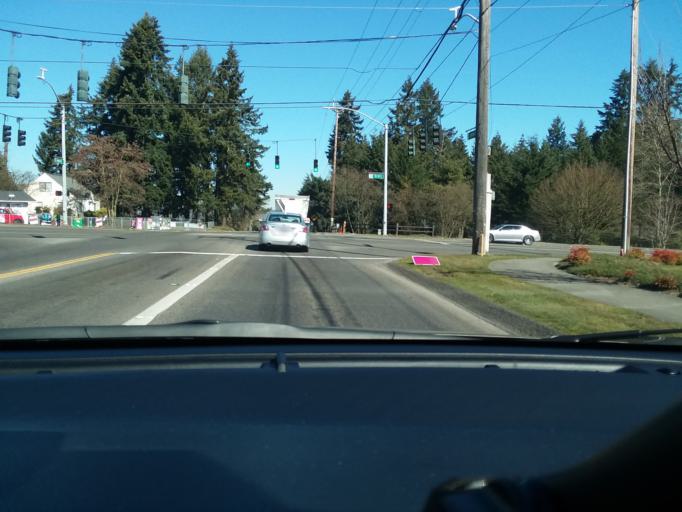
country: US
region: Washington
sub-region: Pierce County
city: Waller
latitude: 47.1915
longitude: -122.3573
